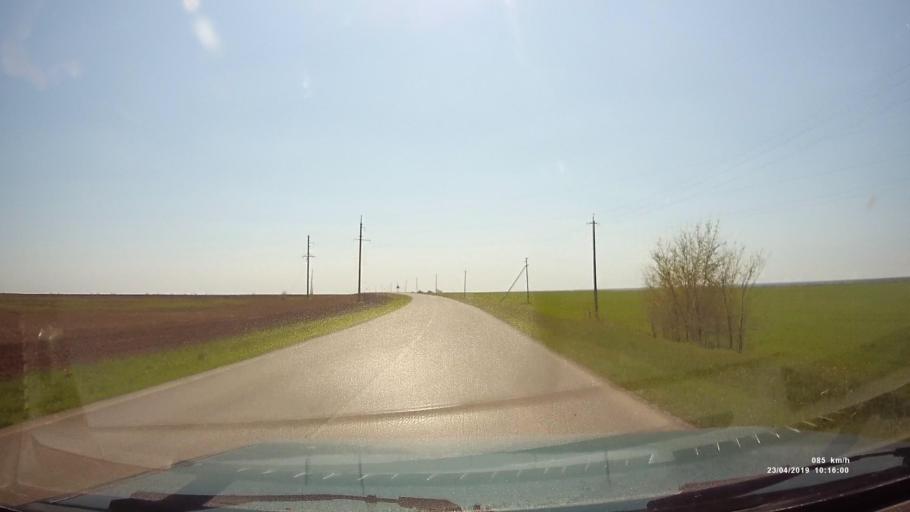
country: RU
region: Rostov
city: Sovetskoye
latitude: 46.6614
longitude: 42.3888
